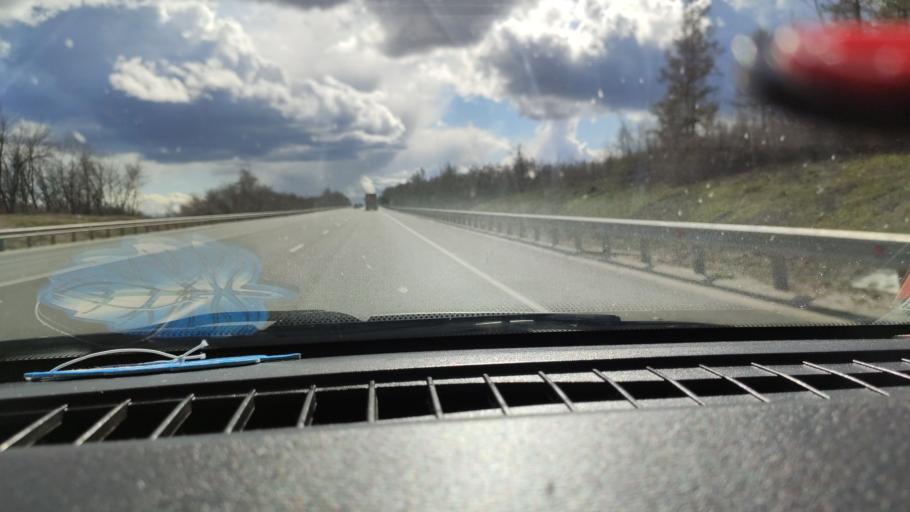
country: RU
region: Saratov
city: Khvalynsk
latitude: 52.5645
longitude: 48.0936
